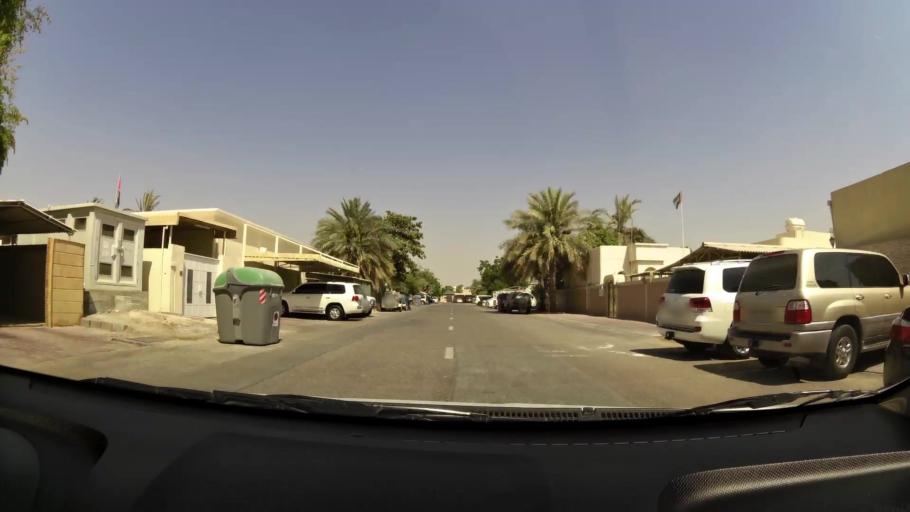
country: AE
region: Ajman
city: Ajman
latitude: 25.4115
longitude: 55.4776
